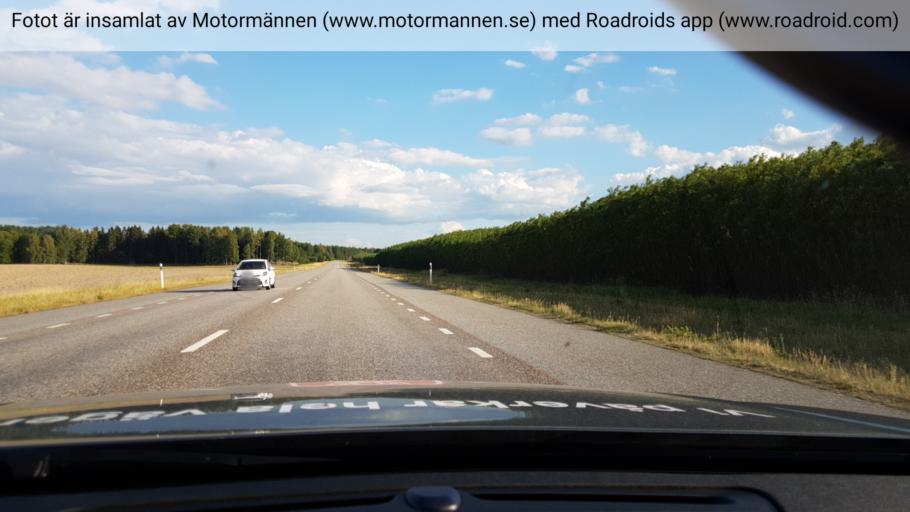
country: SE
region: Uppsala
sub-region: Heby Kommun
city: Morgongava
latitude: 59.8628
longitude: 16.9272
